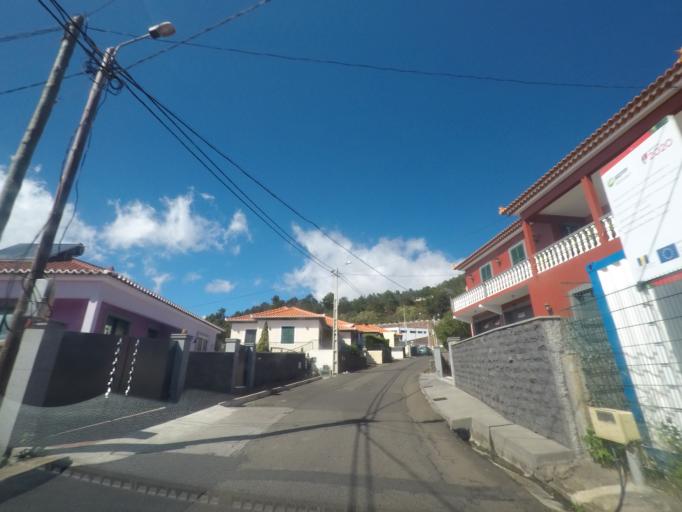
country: PT
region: Madeira
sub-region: Ribeira Brava
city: Campanario
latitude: 32.6795
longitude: -17.0403
